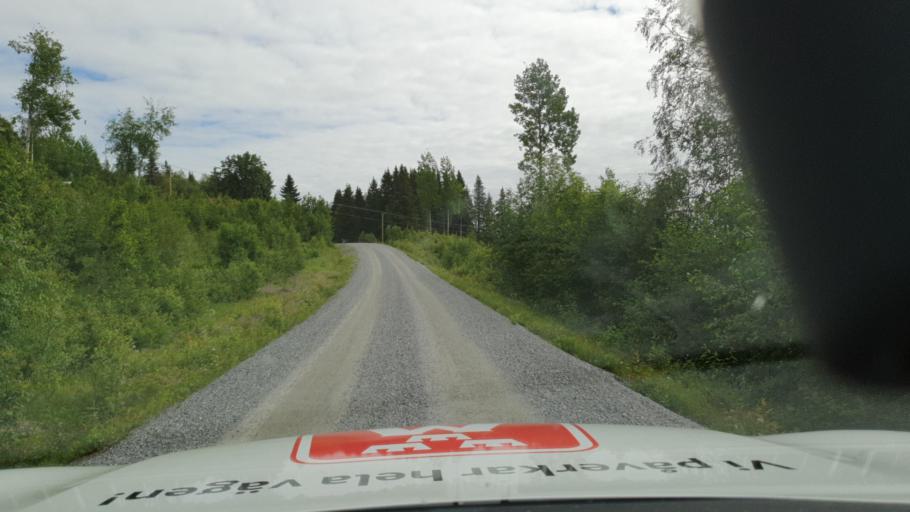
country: SE
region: Vaesterbotten
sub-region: Skelleftea Kommun
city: Langsele
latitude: 64.6470
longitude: 20.2863
